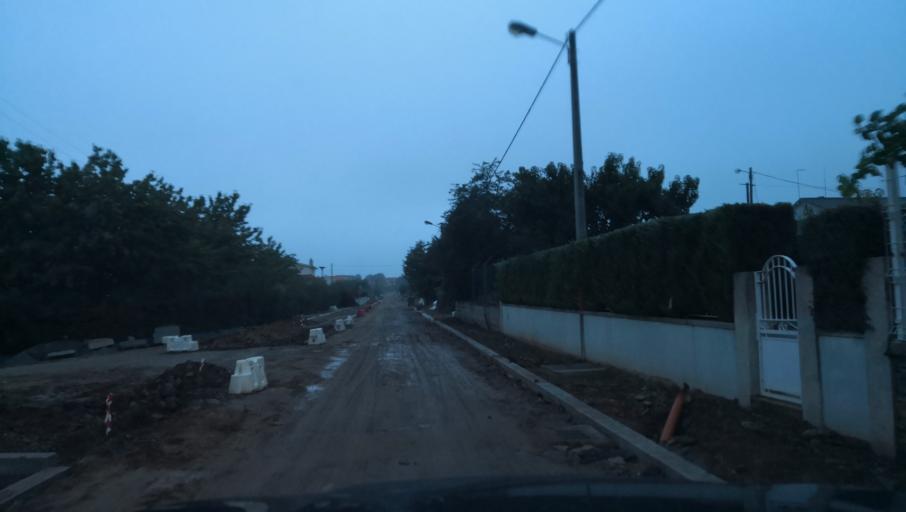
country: PT
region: Vila Real
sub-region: Sabrosa
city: Sabrosa
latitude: 41.2644
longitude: -7.6125
